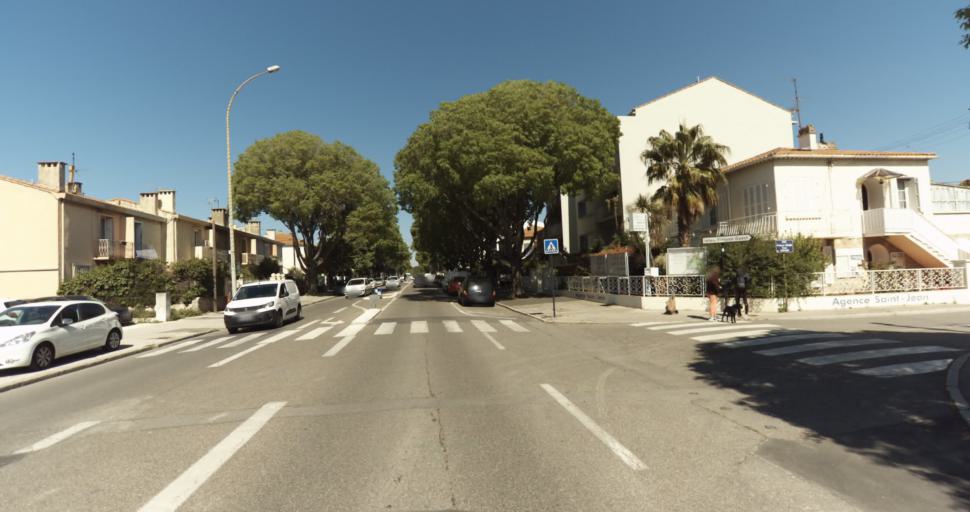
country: FR
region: Provence-Alpes-Cote d'Azur
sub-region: Departement du Var
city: La Seyne-sur-Mer
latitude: 43.1055
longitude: 5.8683
